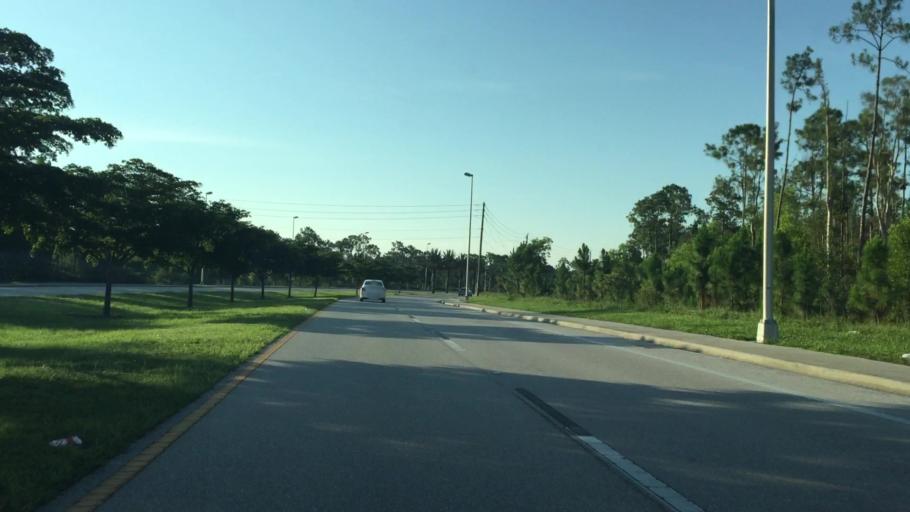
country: US
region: Florida
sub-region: Lee County
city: Three Oaks
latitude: 26.4667
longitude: -81.7916
